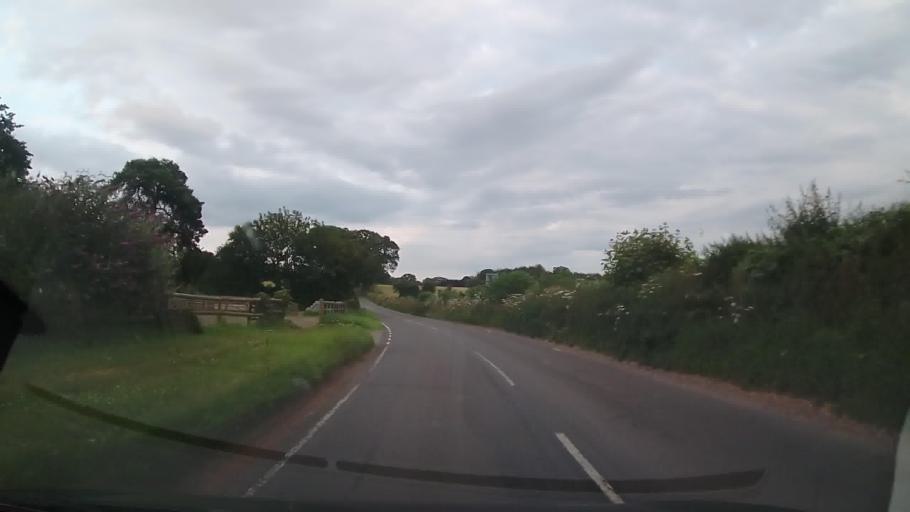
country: GB
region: England
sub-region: Shropshire
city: Great Ness
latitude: 52.7991
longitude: -2.9381
